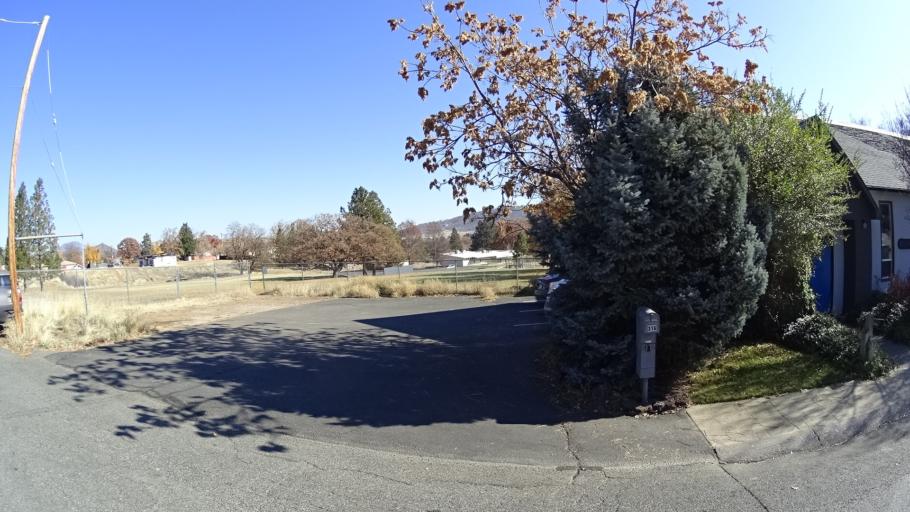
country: US
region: California
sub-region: Siskiyou County
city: Yreka
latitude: 41.7359
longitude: -122.6425
